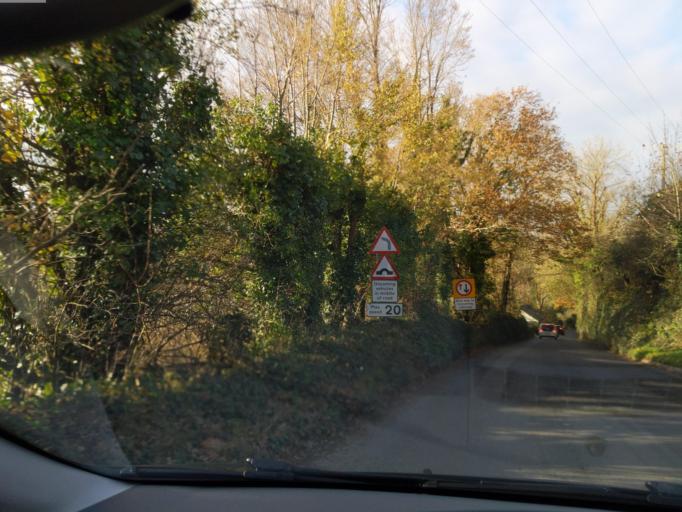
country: GB
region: England
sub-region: Cornwall
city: Padstow
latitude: 50.5113
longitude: -4.9347
